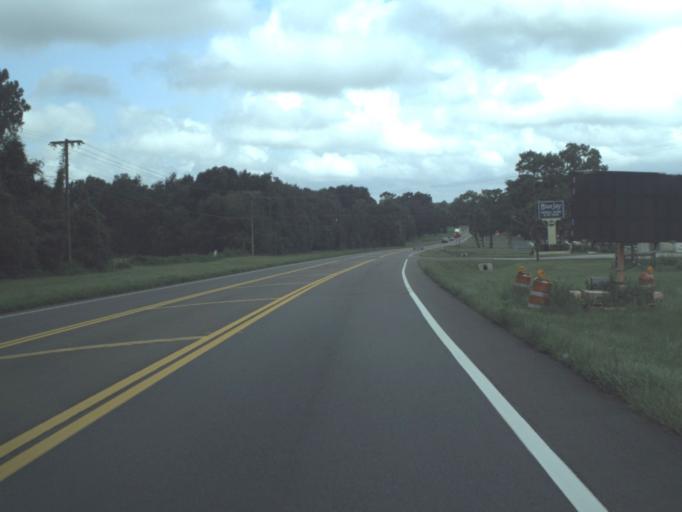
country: US
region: Florida
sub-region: Pasco County
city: Dade City
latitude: 28.3167
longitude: -82.1785
